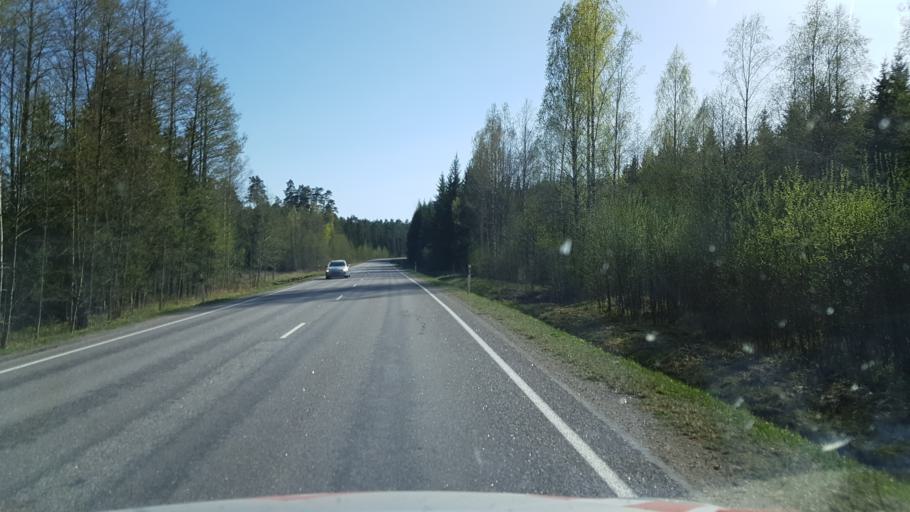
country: EE
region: Viljandimaa
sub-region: Moisakuela linn
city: Moisakula
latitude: 58.2349
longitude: 25.1188
